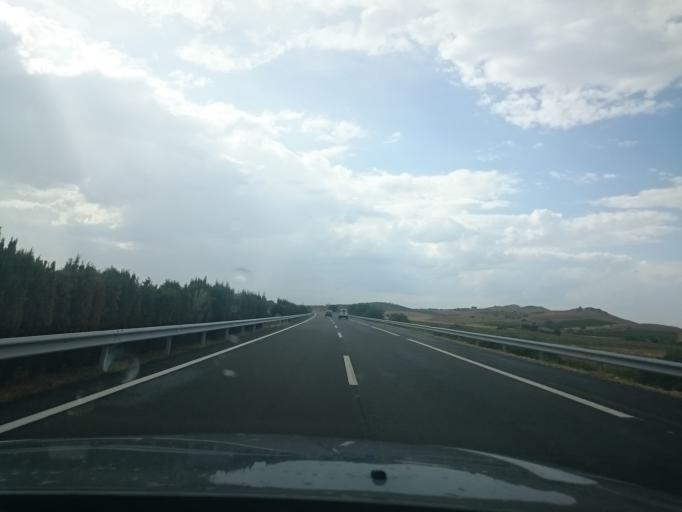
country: ES
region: Navarre
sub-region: Provincia de Navarra
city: Sartaguda
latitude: 42.3713
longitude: -2.0803
